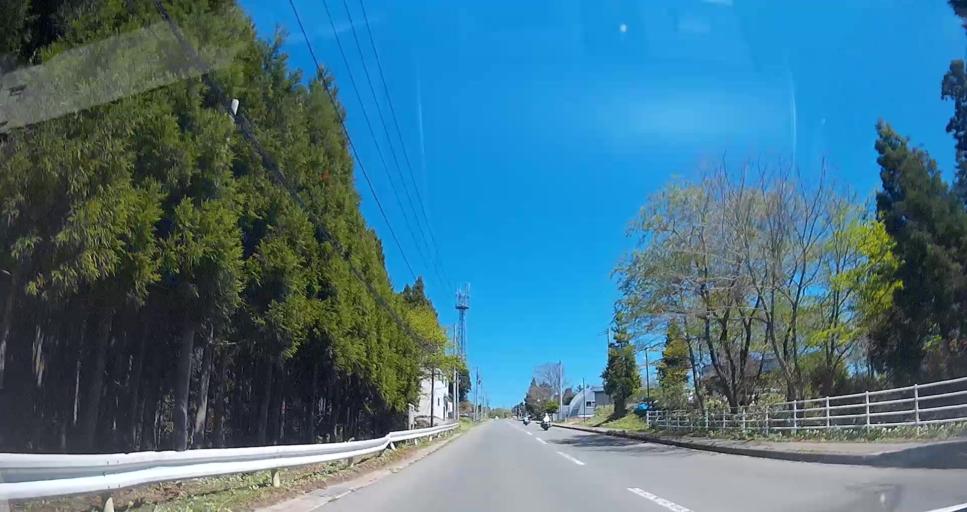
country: JP
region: Aomori
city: Mutsu
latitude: 41.0916
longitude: 141.3892
